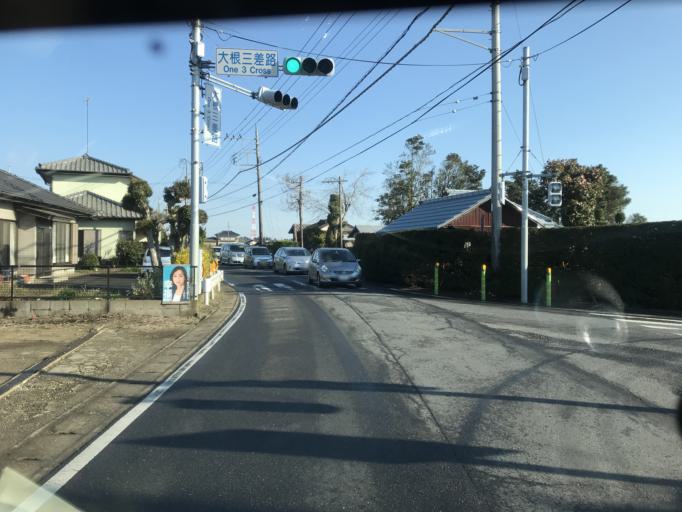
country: JP
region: Chiba
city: Sawara
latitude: 35.8532
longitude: 140.5085
